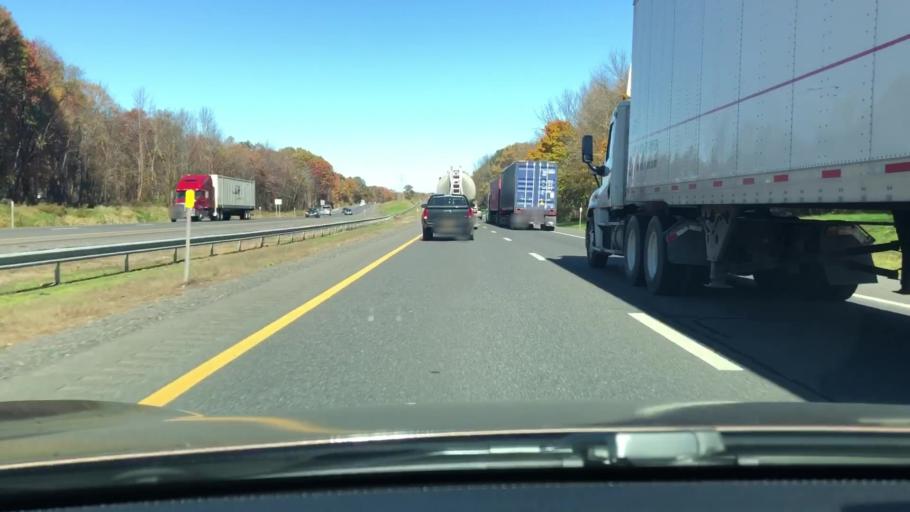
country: US
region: New York
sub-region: Ulster County
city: Clintondale
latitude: 41.7115
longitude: -74.0741
